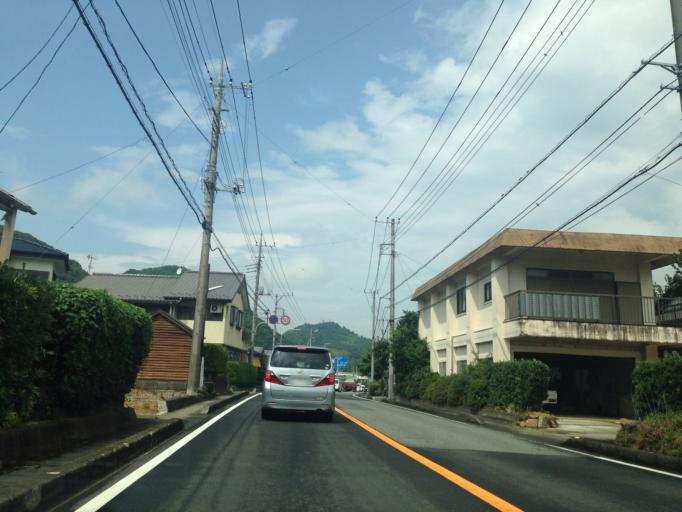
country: JP
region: Shizuoka
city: Ito
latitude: 34.9579
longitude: 138.9366
